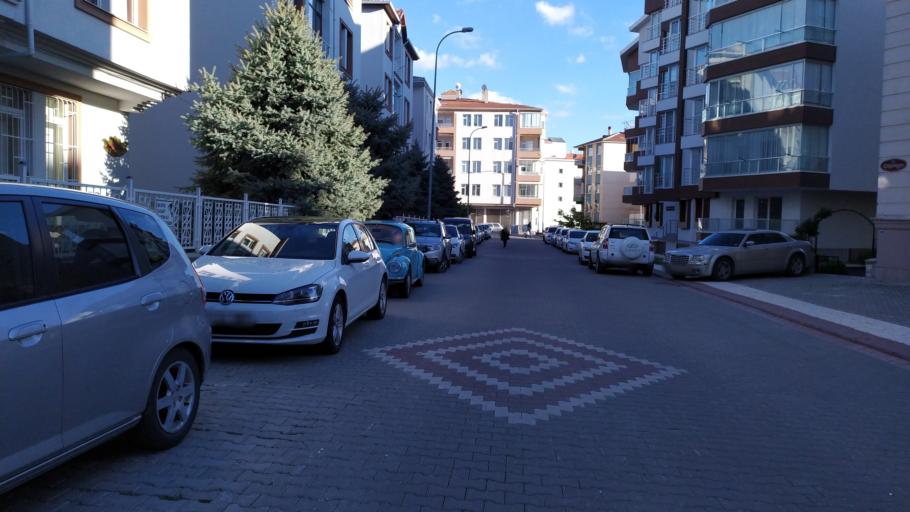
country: TR
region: Kirsehir
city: Kirsehir
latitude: 39.1525
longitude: 34.1585
